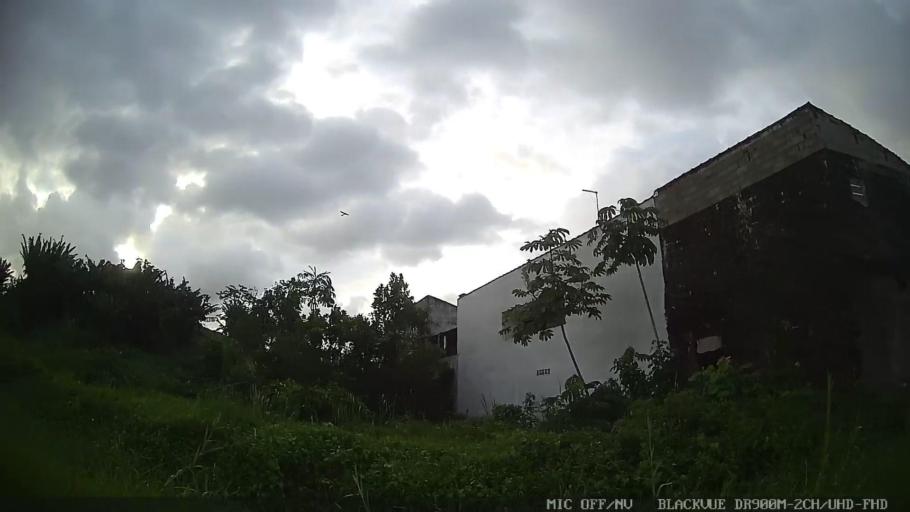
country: BR
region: Sao Paulo
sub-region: Itanhaem
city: Itanhaem
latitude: -24.1732
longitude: -46.7714
